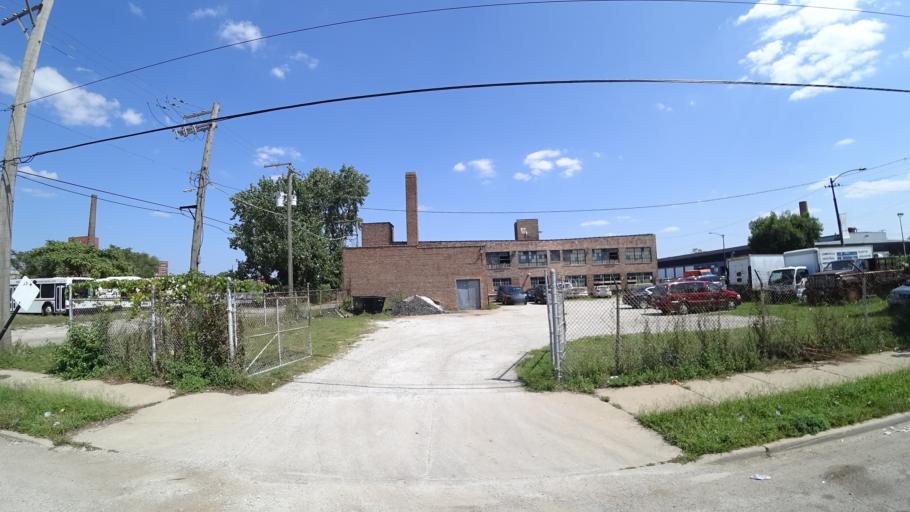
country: US
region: Illinois
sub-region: Cook County
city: Cicero
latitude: 41.8663
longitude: -87.7374
